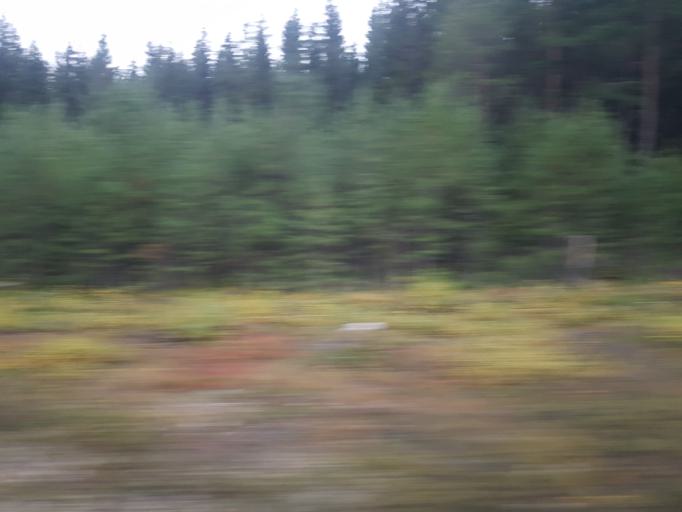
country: NO
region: Oppland
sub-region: Dovre
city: Dovre
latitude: 61.9219
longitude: 9.3378
